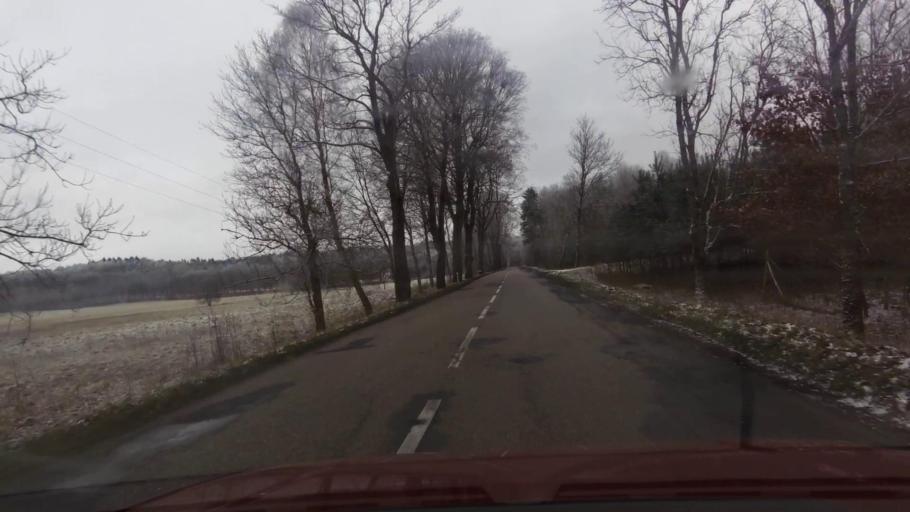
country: PL
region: West Pomeranian Voivodeship
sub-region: Powiat swidwinski
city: Polczyn-Zdroj
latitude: 53.7930
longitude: 16.0510
